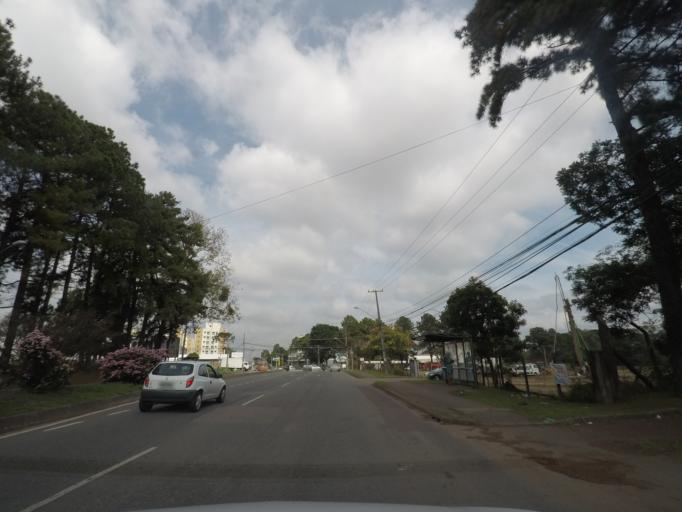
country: BR
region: Parana
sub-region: Curitiba
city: Curitiba
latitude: -25.4943
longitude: -49.3247
